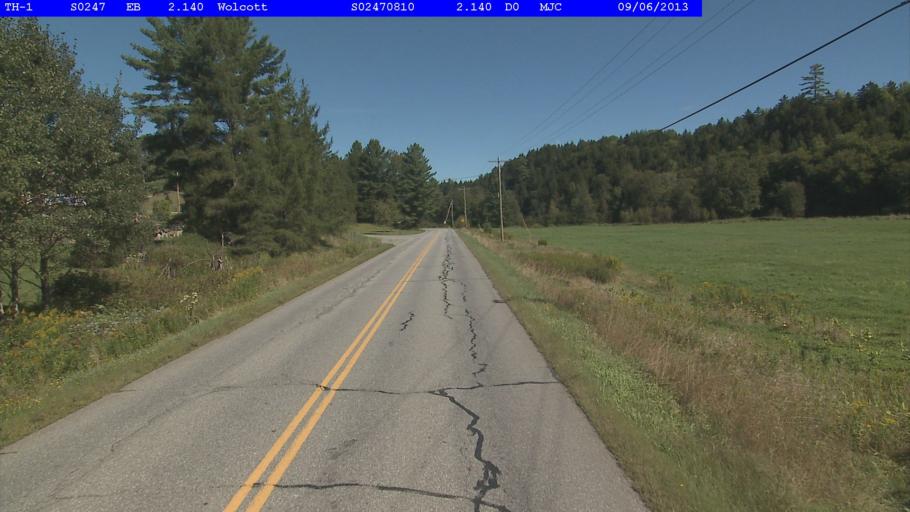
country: US
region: Vermont
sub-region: Lamoille County
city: Morrisville
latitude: 44.5864
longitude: -72.4742
